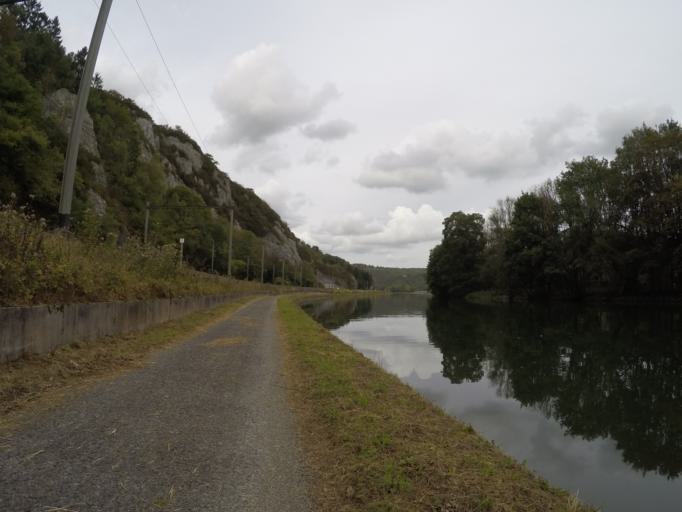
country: BE
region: Wallonia
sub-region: Province de Namur
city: Anhee
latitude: 50.2874
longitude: 4.8909
